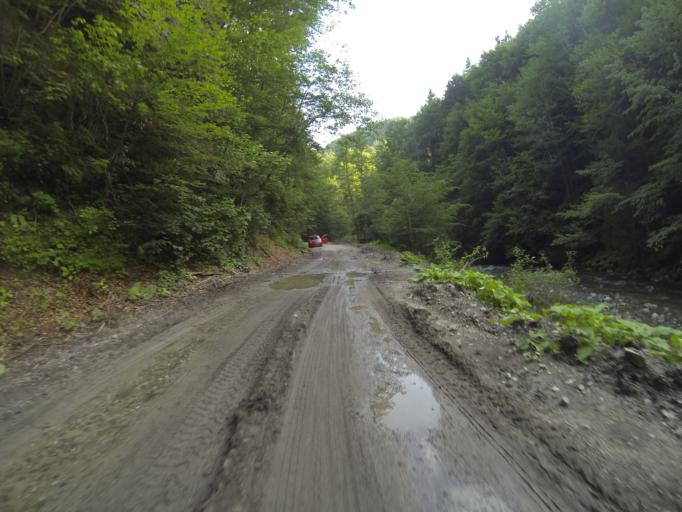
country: RO
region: Valcea
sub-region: Oras Baile Olanesti
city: Baile Olanesti
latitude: 45.2295
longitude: 24.2056
